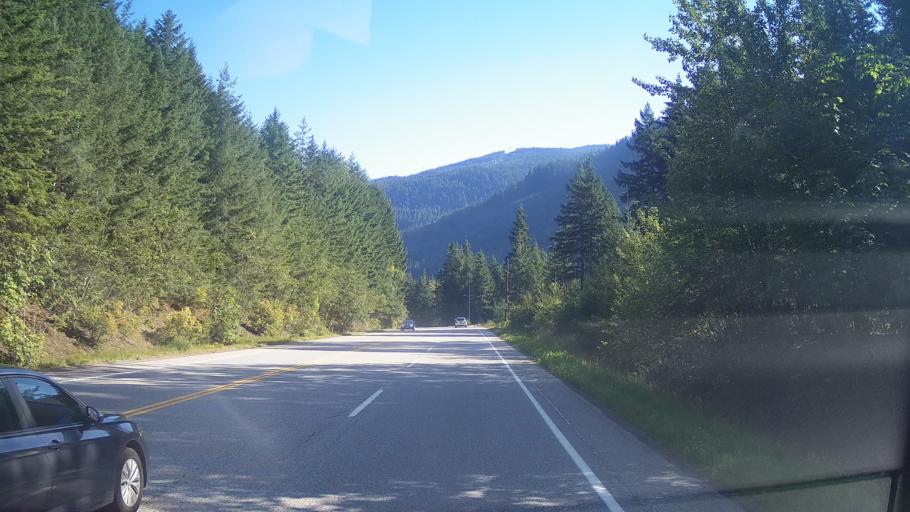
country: CA
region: British Columbia
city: Hope
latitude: 49.6469
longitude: -121.4100
